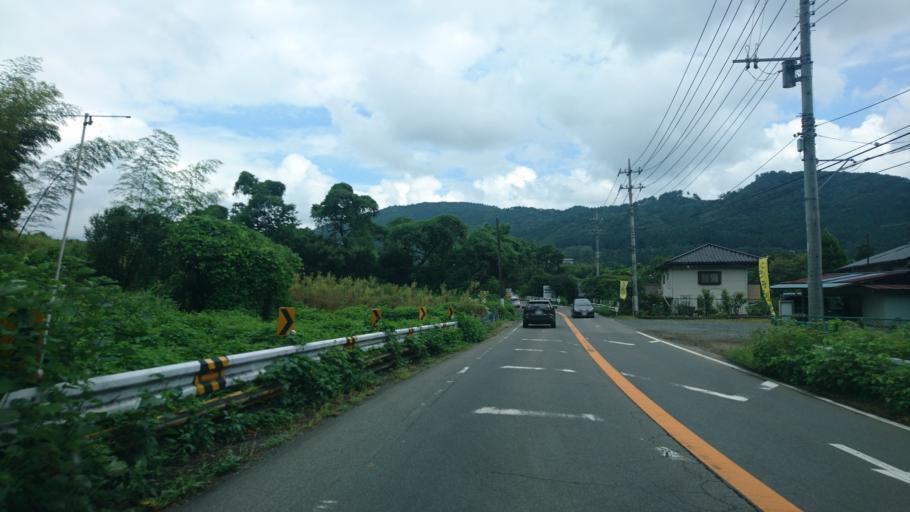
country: JP
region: Gunma
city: Omamacho-omama
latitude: 36.4578
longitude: 139.2634
